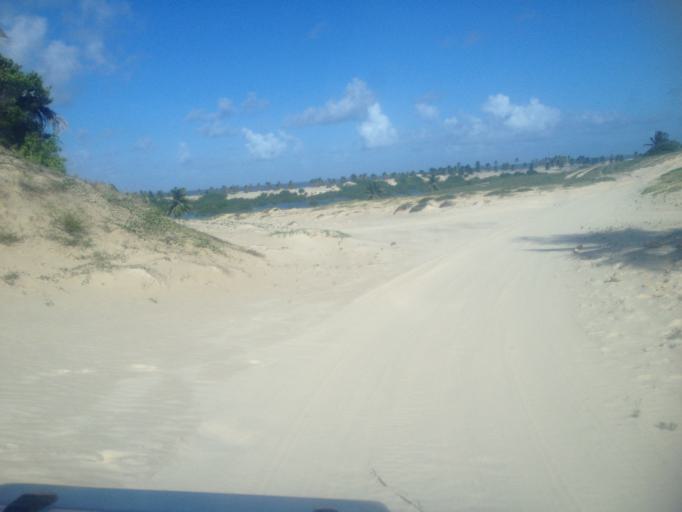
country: BR
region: Sergipe
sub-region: Indiaroba
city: Indiaroba
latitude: -11.4685
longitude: -37.3676
